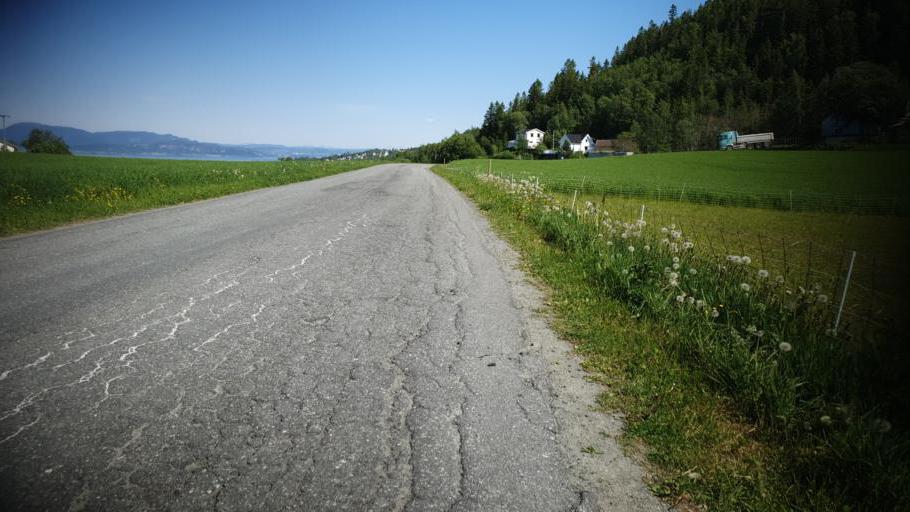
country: NO
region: Sor-Trondelag
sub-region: Malvik
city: Malvik
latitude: 63.4320
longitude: 10.5931
